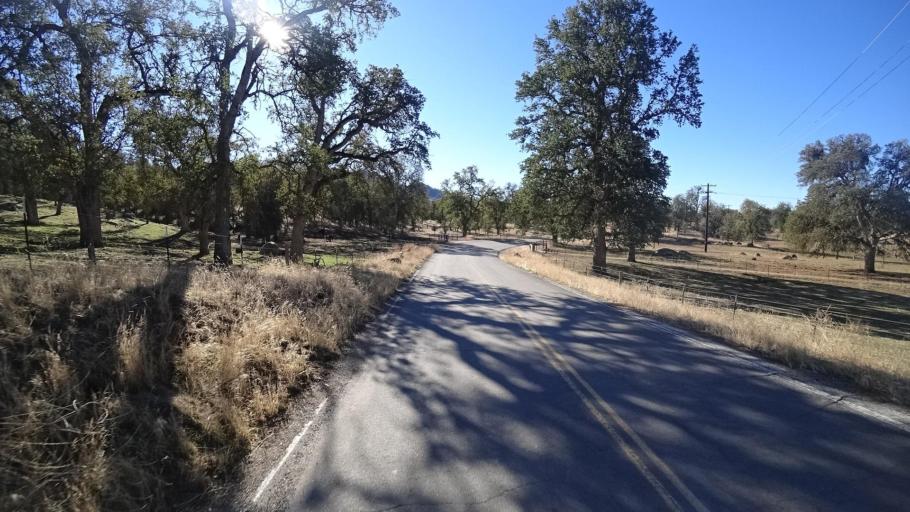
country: US
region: California
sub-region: Kern County
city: Alta Sierra
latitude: 35.7796
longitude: -118.7016
